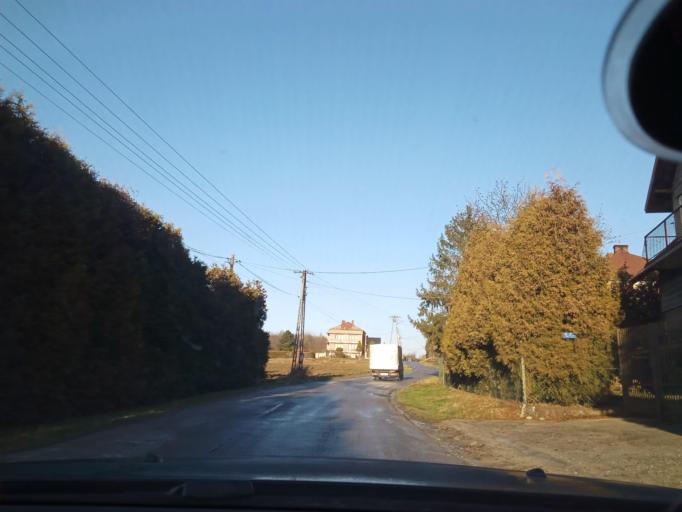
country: PL
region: Lesser Poland Voivodeship
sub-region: Powiat krakowski
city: Michalowice
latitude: 50.1916
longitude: 20.0249
